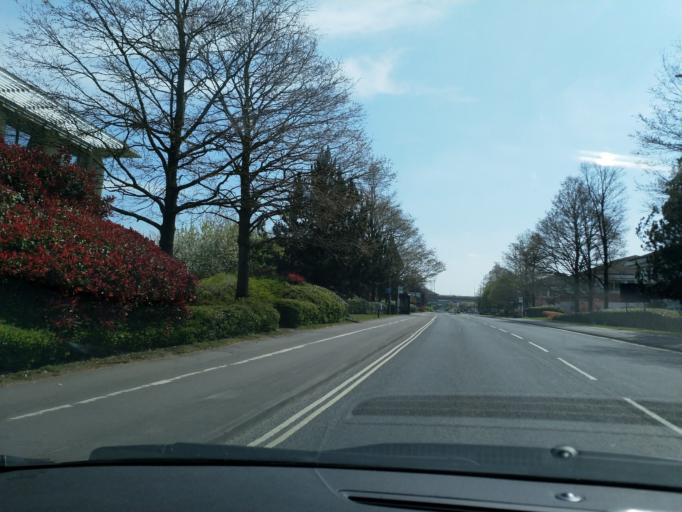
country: GB
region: England
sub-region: Oxfordshire
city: Cowley
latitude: 51.7317
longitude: -1.2057
